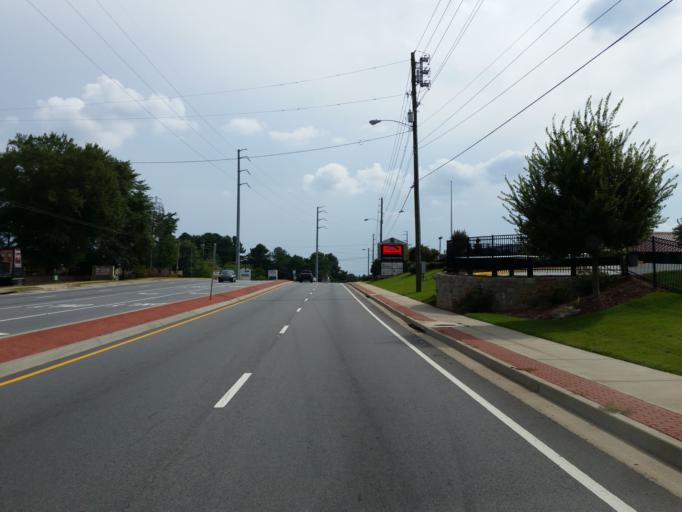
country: US
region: Georgia
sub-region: Cobb County
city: Marietta
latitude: 34.0124
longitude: -84.4961
